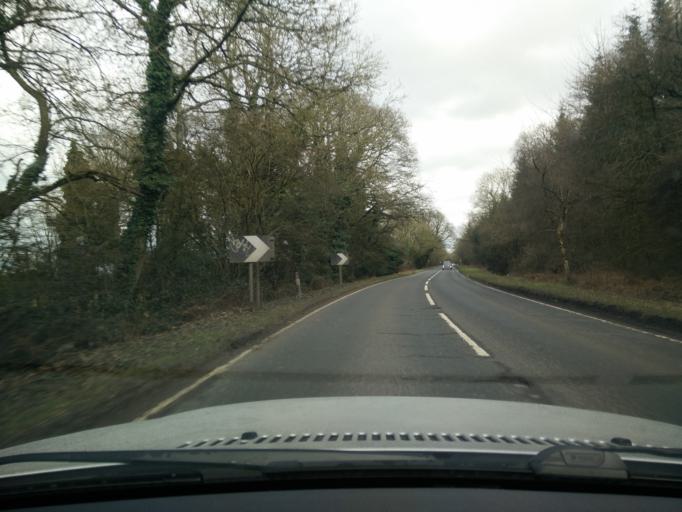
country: GB
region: England
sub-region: Buckinghamshire
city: Great Missenden
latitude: 51.6618
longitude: -0.6759
